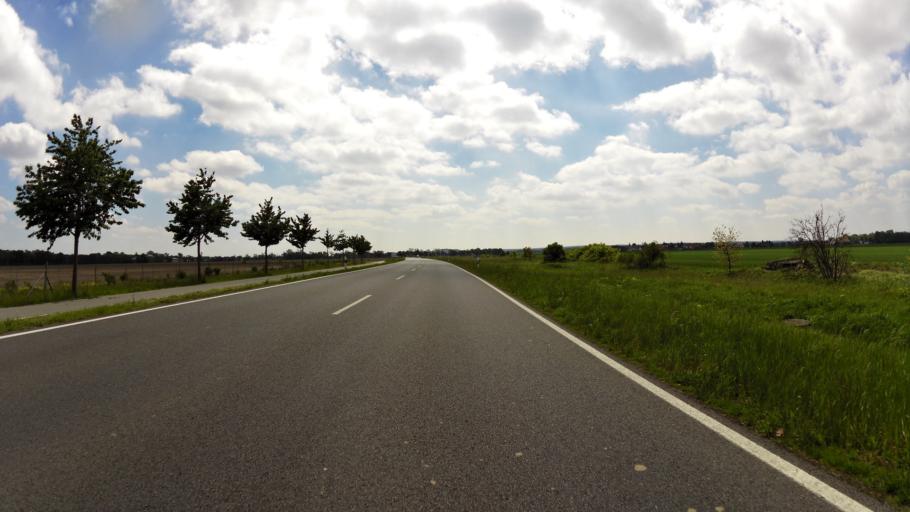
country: DE
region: Saxony
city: Torgau
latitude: 51.5213
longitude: 13.0311
